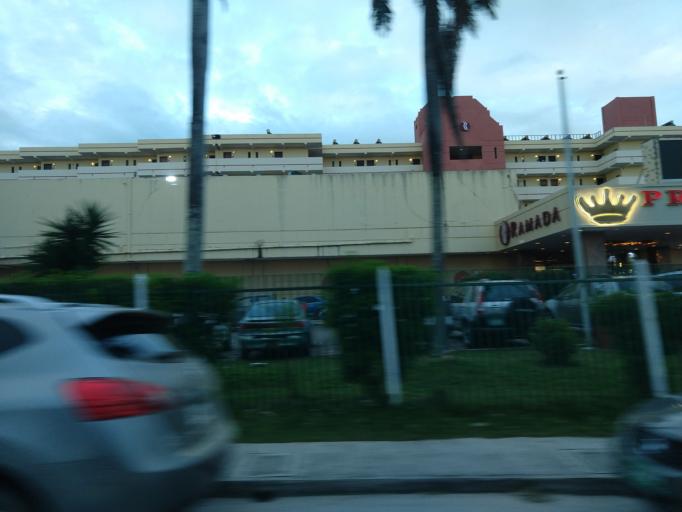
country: BZ
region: Belize
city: Belize City
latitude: 17.5052
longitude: -88.1886
